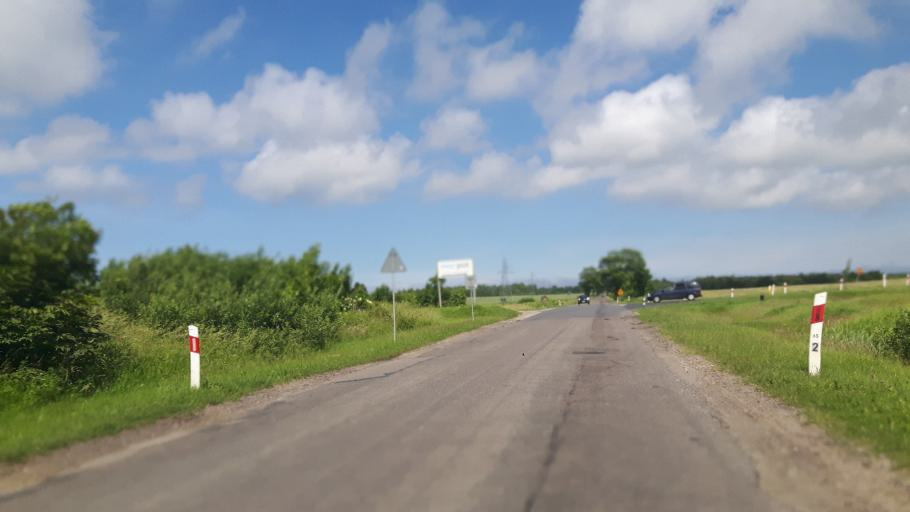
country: PL
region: Pomeranian Voivodeship
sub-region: Powiat slupski
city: Ustka
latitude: 54.5525
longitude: 16.8363
